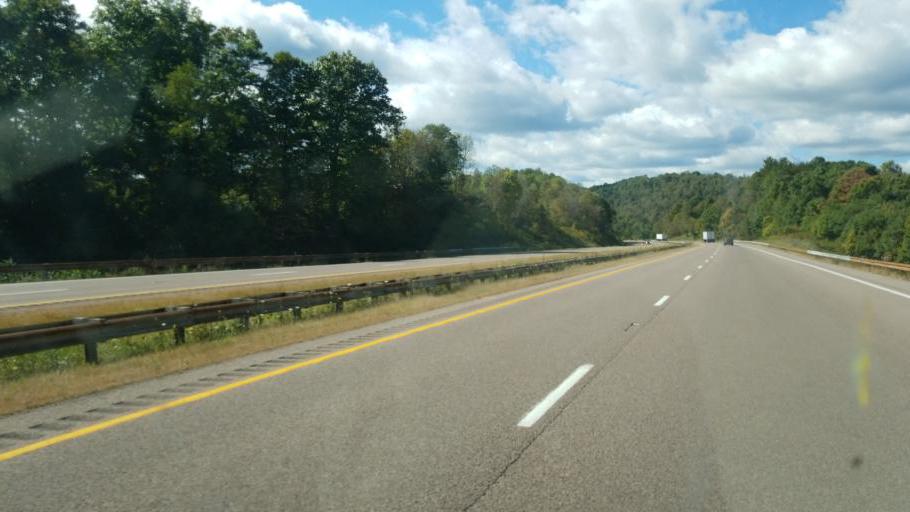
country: US
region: West Virginia
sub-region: Preston County
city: Terra Alta
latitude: 39.6549
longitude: -79.4449
